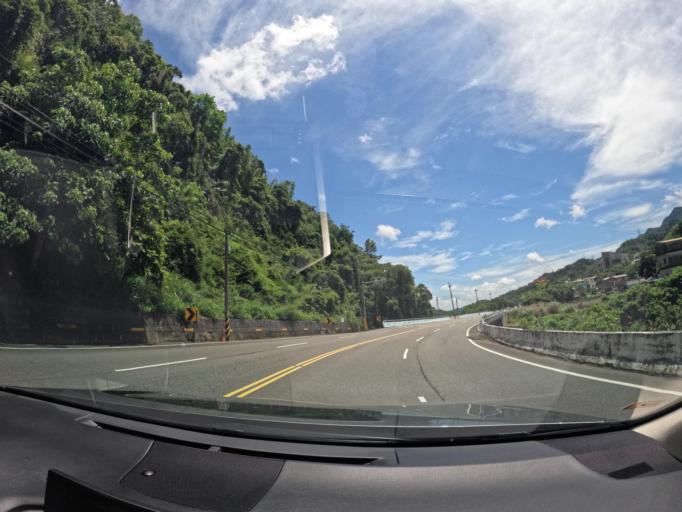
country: TW
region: Taiwan
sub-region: Miaoli
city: Miaoli
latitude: 24.5382
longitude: 120.9179
